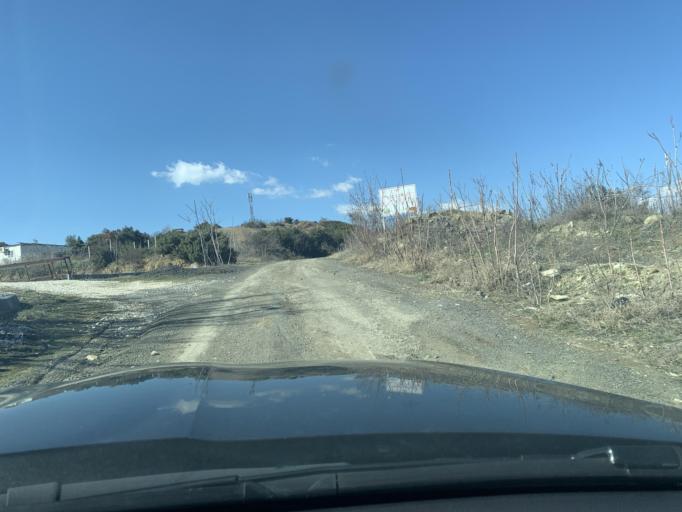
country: MK
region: Demir Kapija
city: Demir Kapija
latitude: 41.4110
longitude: 22.2263
